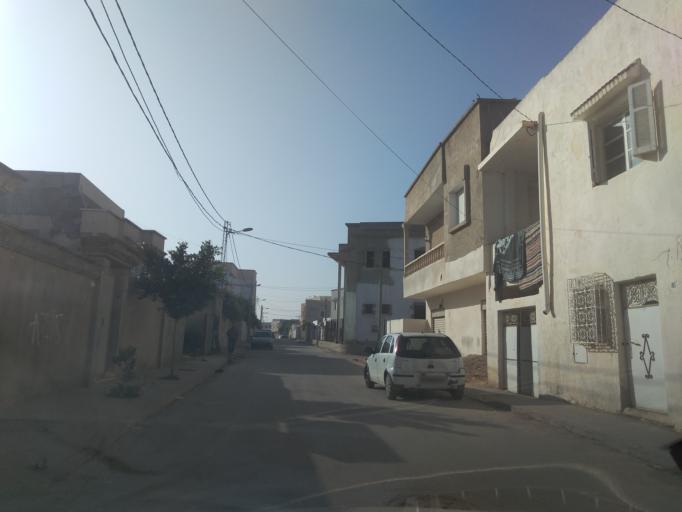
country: TN
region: Manouba
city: Manouba
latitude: 36.7917
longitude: 10.0880
